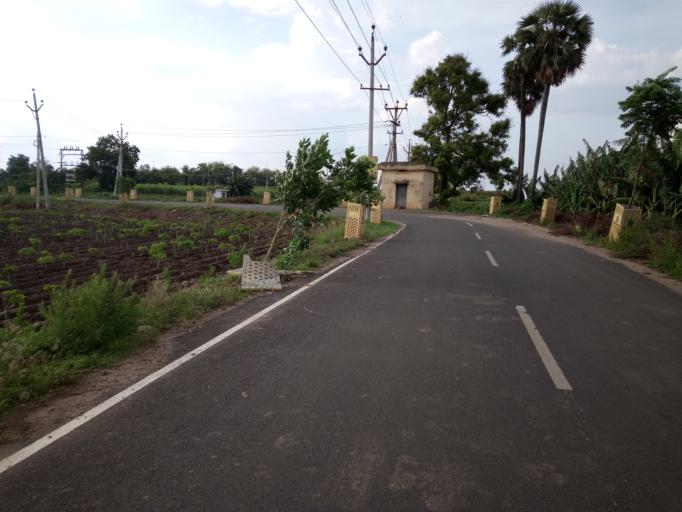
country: IN
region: Andhra Pradesh
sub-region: Guntur
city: Tadepalle
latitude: 16.5022
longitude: 80.5820
